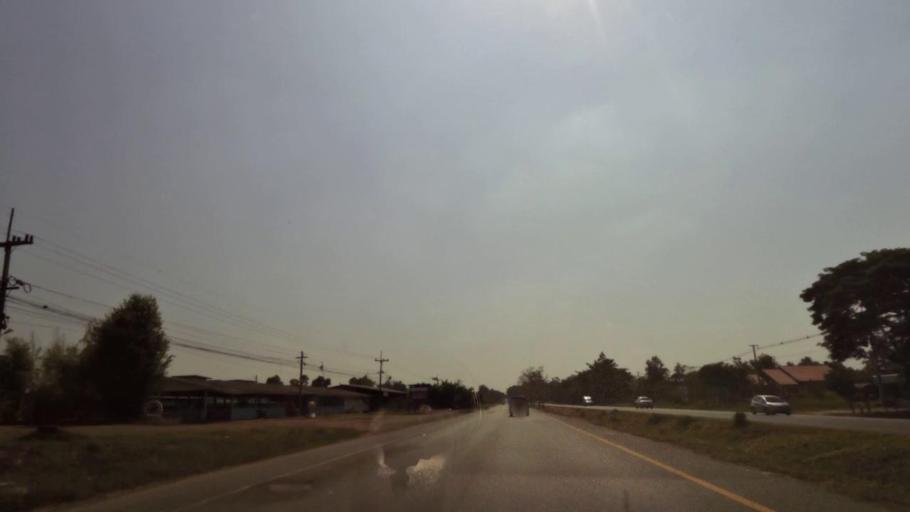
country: TH
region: Phichit
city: Bueng Na Rang
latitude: 16.3431
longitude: 100.1283
